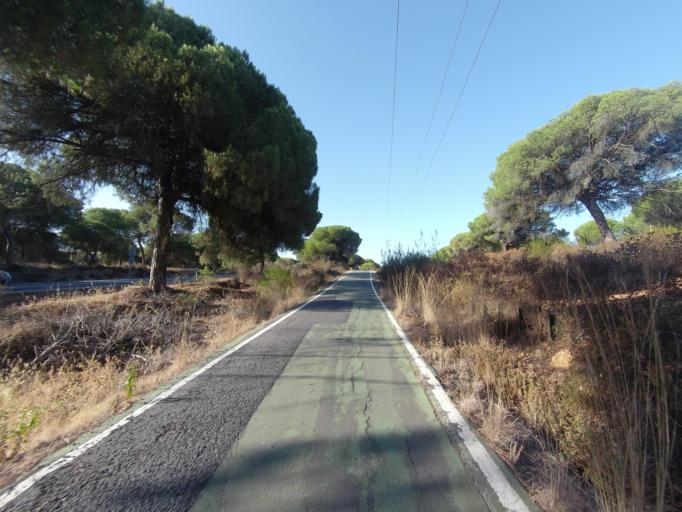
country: ES
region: Andalusia
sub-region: Provincia de Huelva
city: Aljaraque
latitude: 37.2146
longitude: -7.0269
